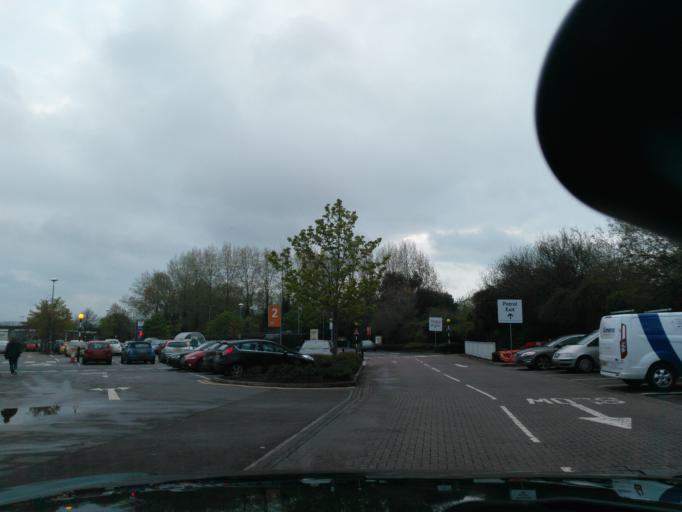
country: GB
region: England
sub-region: Wiltshire
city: Trowbridge
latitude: 51.3171
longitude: -2.2013
